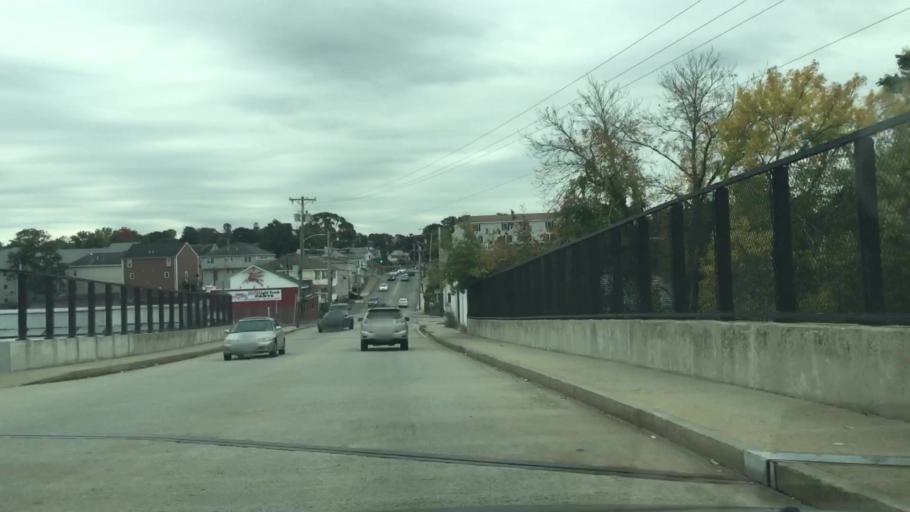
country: US
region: Massachusetts
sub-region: Middlesex County
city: Lowell
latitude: 42.6408
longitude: -71.3253
